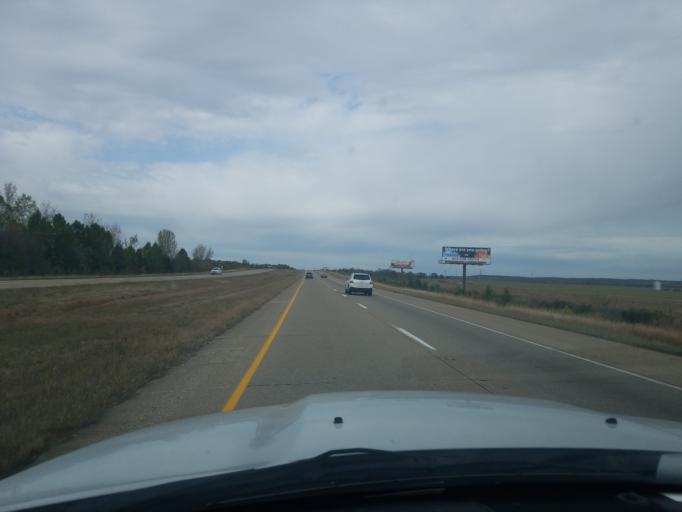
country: US
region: Indiana
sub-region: Vanderburgh County
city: Melody Hill
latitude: 38.0457
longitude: -87.4741
